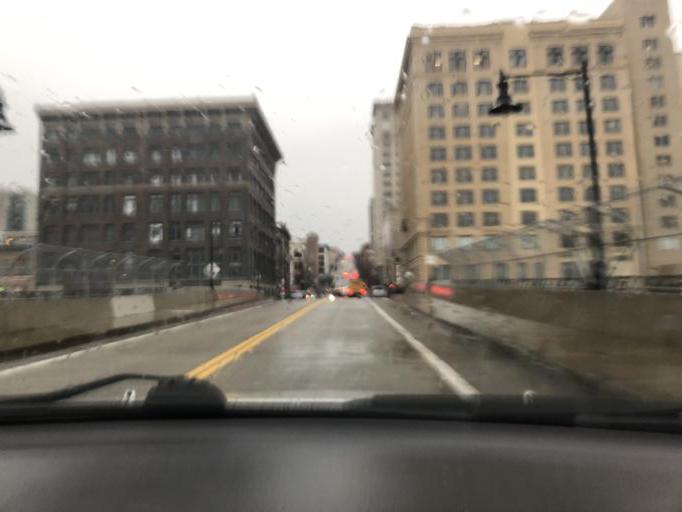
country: US
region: Washington
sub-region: Pierce County
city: Tacoma
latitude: 47.2537
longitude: -122.4356
